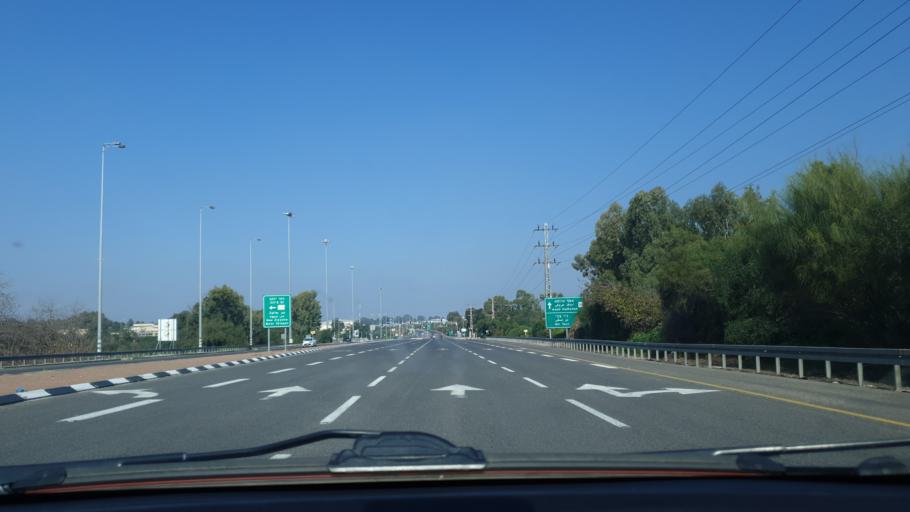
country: IL
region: Central District
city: Ramla
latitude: 31.9492
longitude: 34.8578
